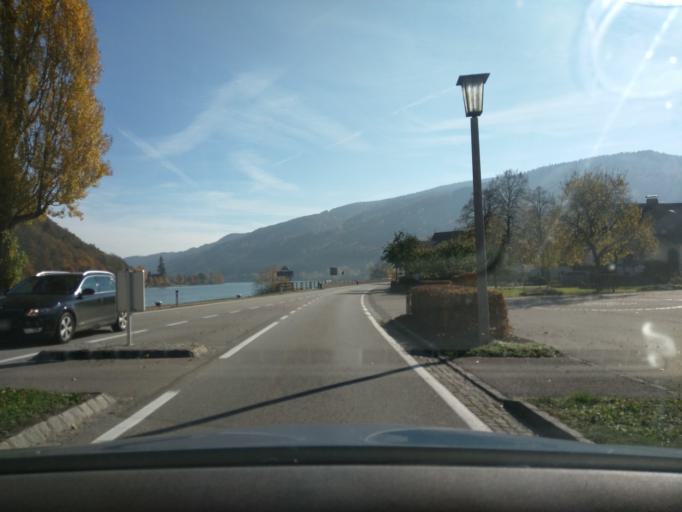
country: DE
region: Bavaria
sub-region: Lower Bavaria
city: Obernzell
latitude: 48.5428
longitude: 13.6555
